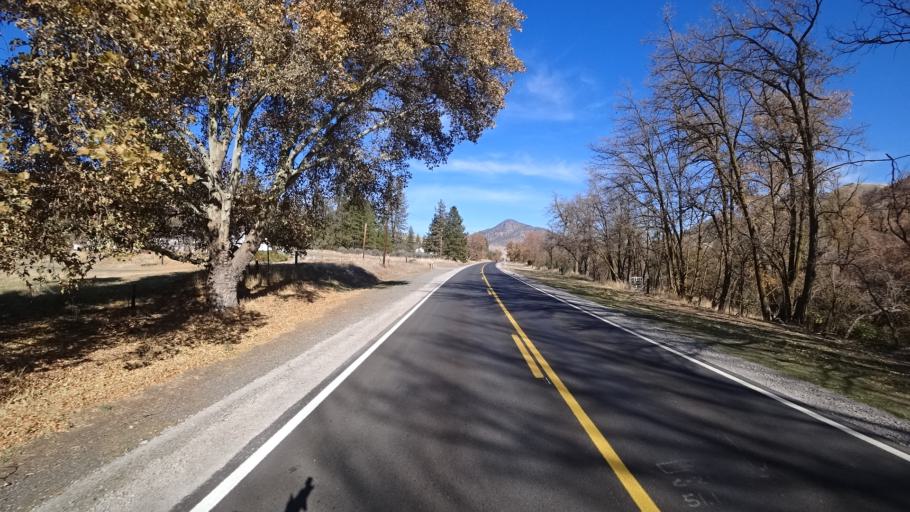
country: US
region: California
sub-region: Siskiyou County
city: Yreka
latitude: 41.7664
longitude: -122.6156
